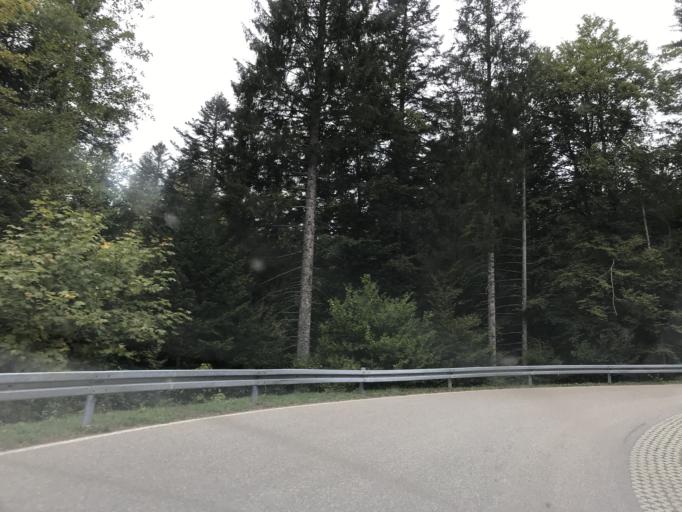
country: DE
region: Baden-Wuerttemberg
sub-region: Freiburg Region
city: Todtmoos
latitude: 47.7191
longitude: 7.9923
